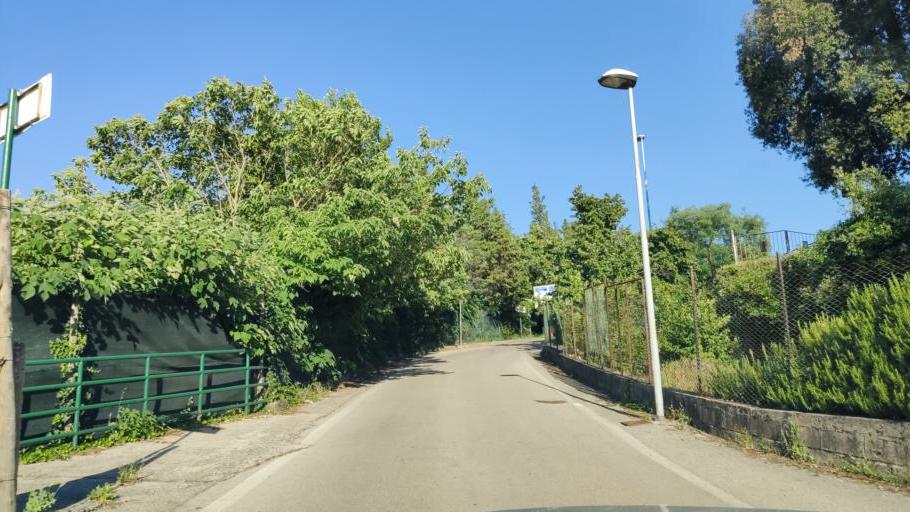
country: IT
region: Umbria
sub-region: Provincia di Terni
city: Narni
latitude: 42.5177
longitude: 12.5218
